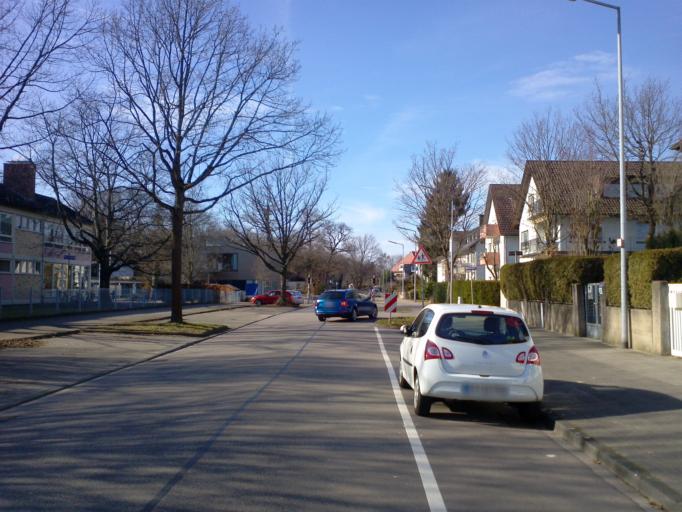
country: DE
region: Baden-Wuerttemberg
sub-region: Karlsruhe Region
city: Karlsruhe
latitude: 48.9803
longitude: 8.3932
